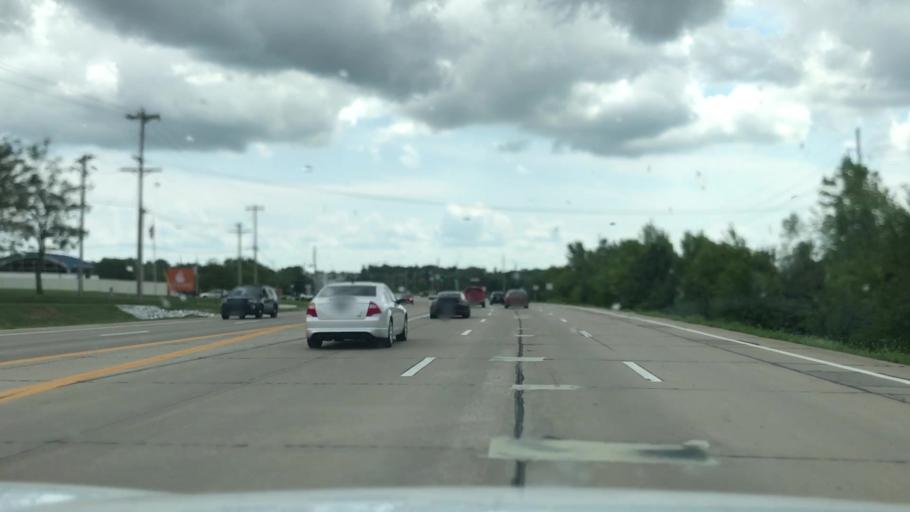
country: US
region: Missouri
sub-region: Saint Charles County
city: Weldon Spring
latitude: 38.7474
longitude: -90.6994
